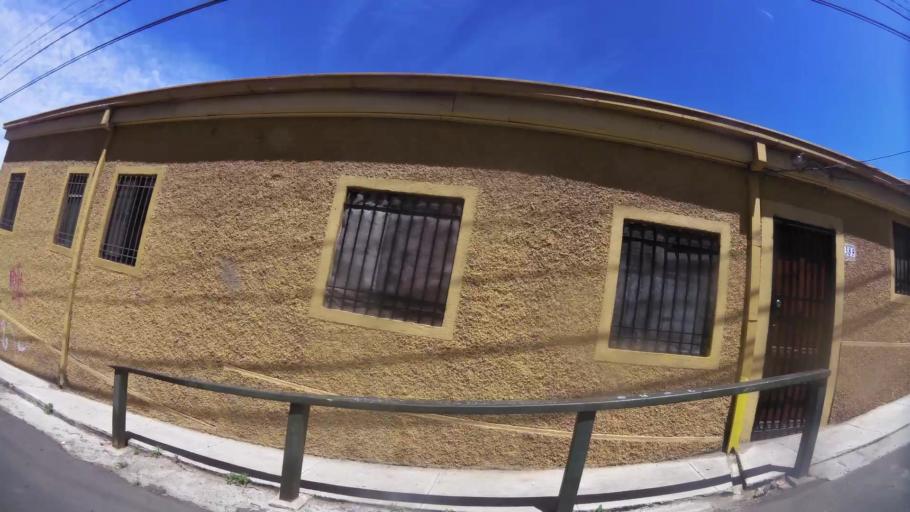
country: CL
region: Valparaiso
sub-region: Provincia de Valparaiso
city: Valparaiso
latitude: -33.0477
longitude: -71.6017
